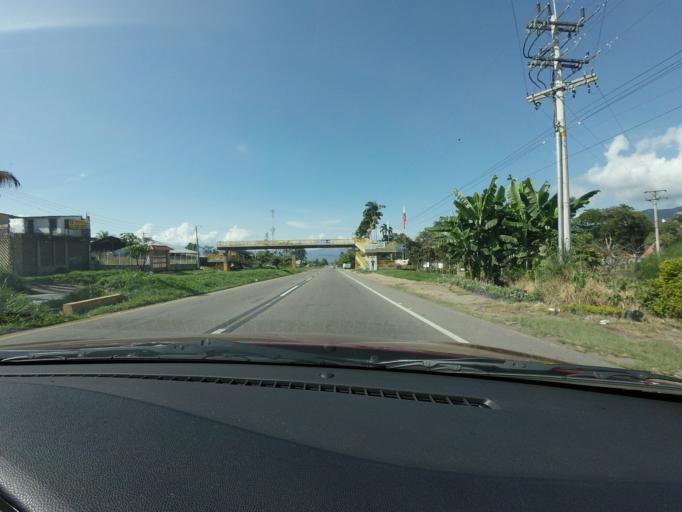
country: CO
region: Cundinamarca
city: Arbelaez
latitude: 4.3119
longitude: -74.4382
